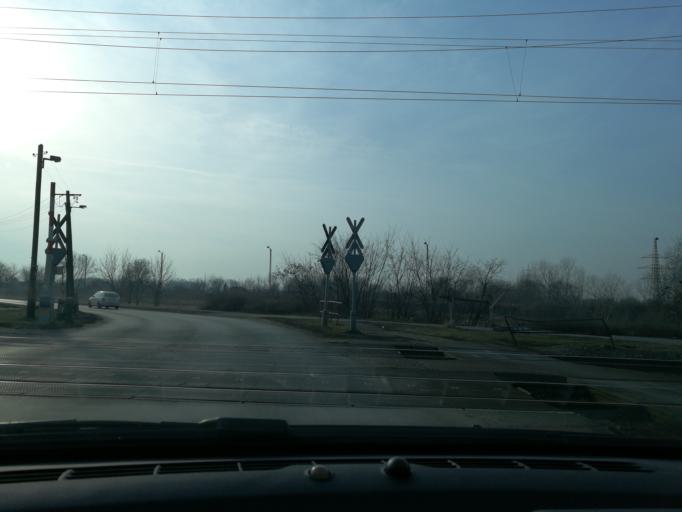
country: HU
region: Szabolcs-Szatmar-Bereg
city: Nyiregyhaza
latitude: 47.9370
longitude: 21.7118
